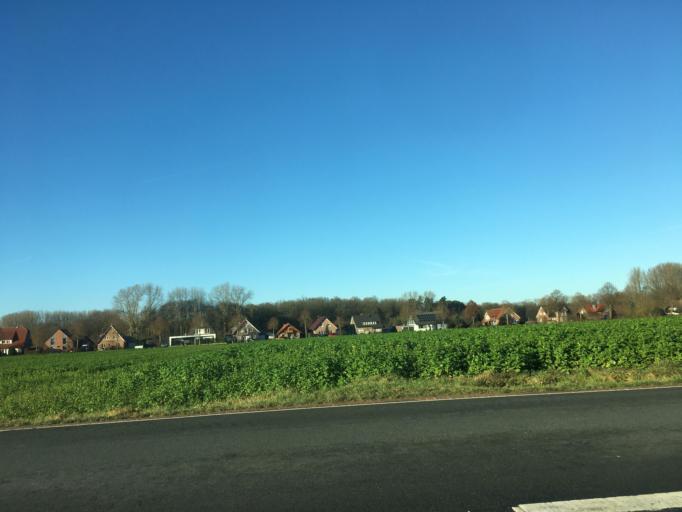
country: DE
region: North Rhine-Westphalia
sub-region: Regierungsbezirk Munster
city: Dulmen
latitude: 51.8645
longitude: 7.2968
